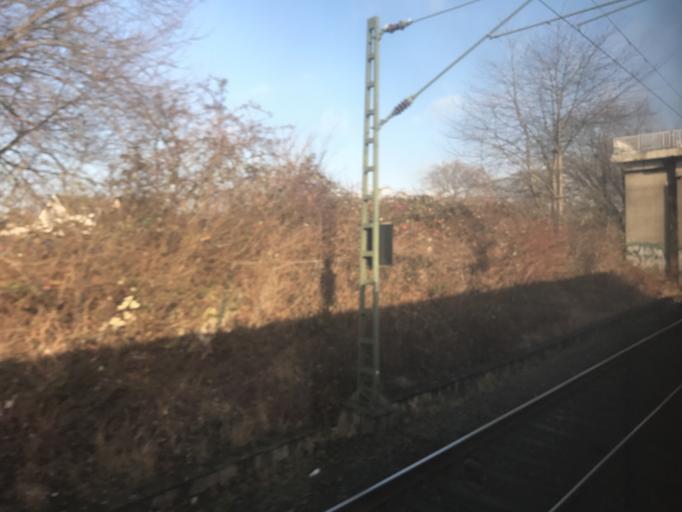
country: DE
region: North Rhine-Westphalia
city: Witten
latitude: 51.5020
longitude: 7.3747
